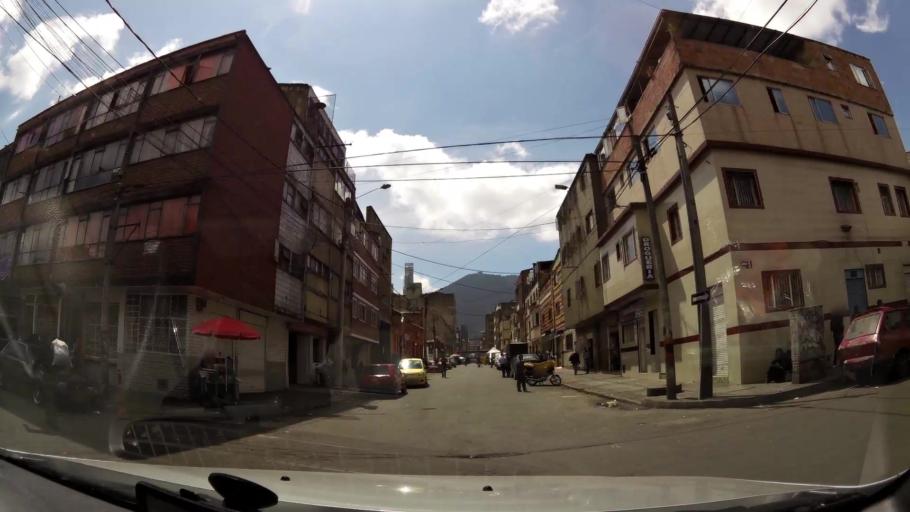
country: CO
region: Bogota D.C.
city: Bogota
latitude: 4.6088
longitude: -74.0783
